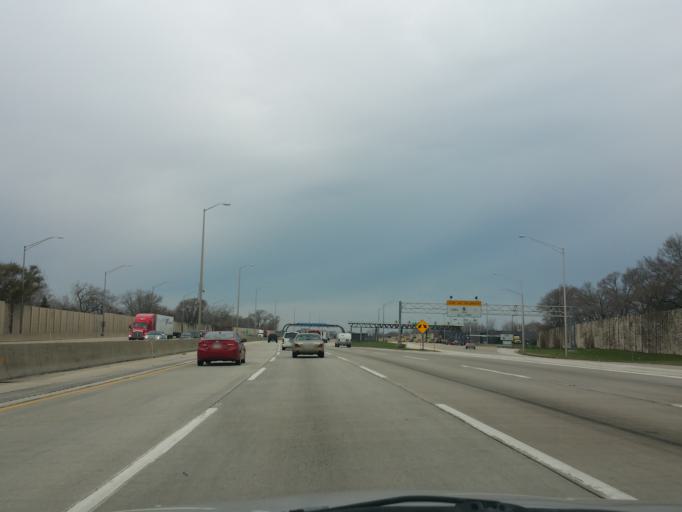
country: US
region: Illinois
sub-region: Cook County
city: Hickory Hills
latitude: 41.7377
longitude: -87.8243
